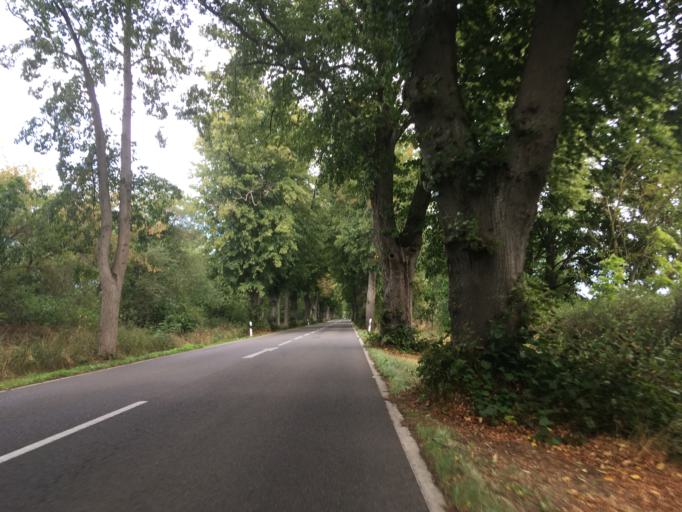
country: DE
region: Brandenburg
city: Templin
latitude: 53.1942
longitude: 13.5625
